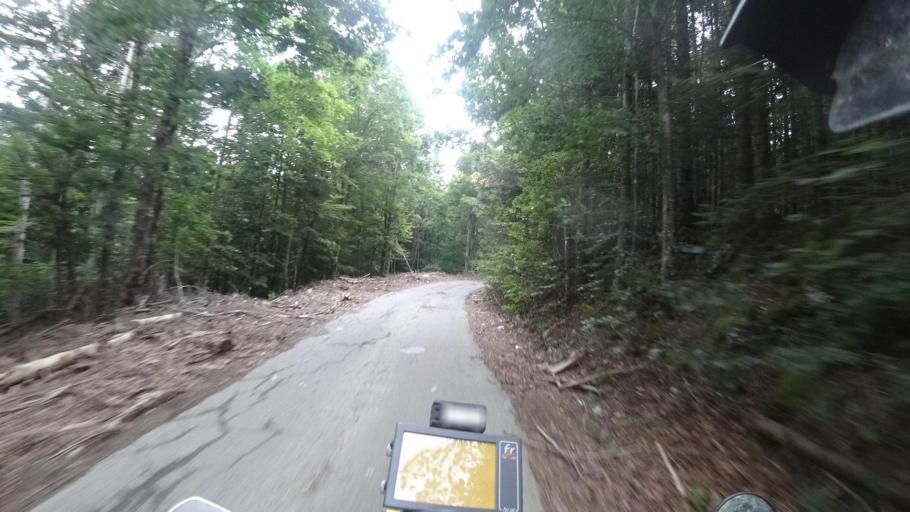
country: HR
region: Licko-Senjska
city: Senj
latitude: 45.1078
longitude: 14.9946
